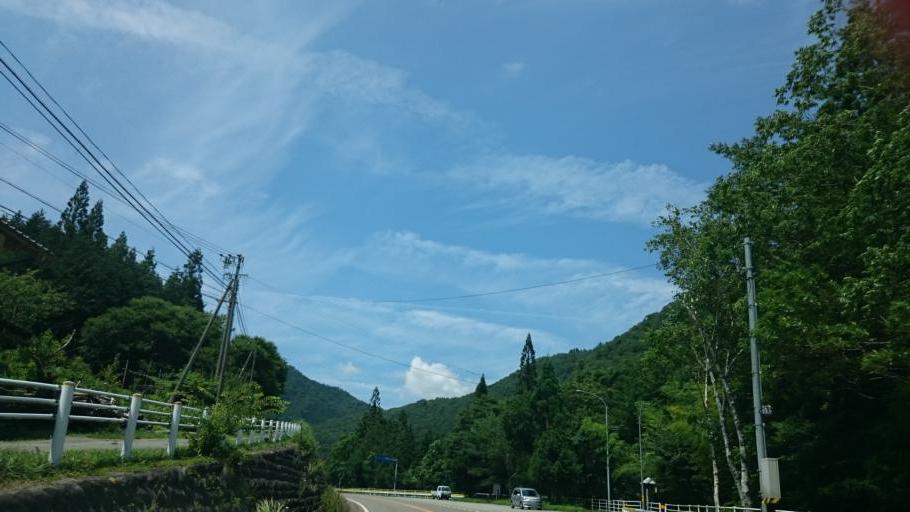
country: JP
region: Gifu
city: Takayama
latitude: 36.0114
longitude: 137.2924
